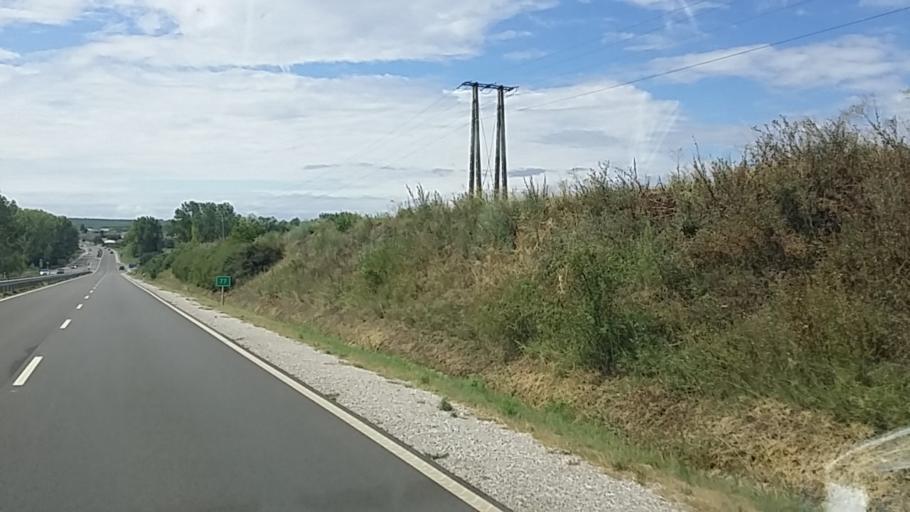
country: HU
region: Heves
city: Nagyrede
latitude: 47.7508
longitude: 19.8842
